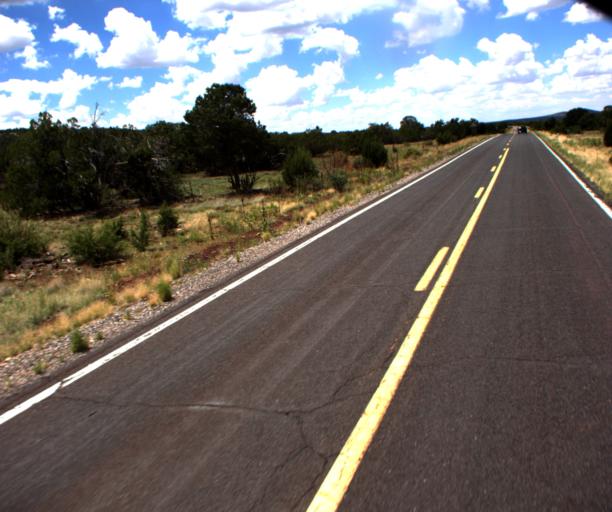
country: US
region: Arizona
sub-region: Coconino County
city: Parks
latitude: 35.5601
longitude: -111.8793
